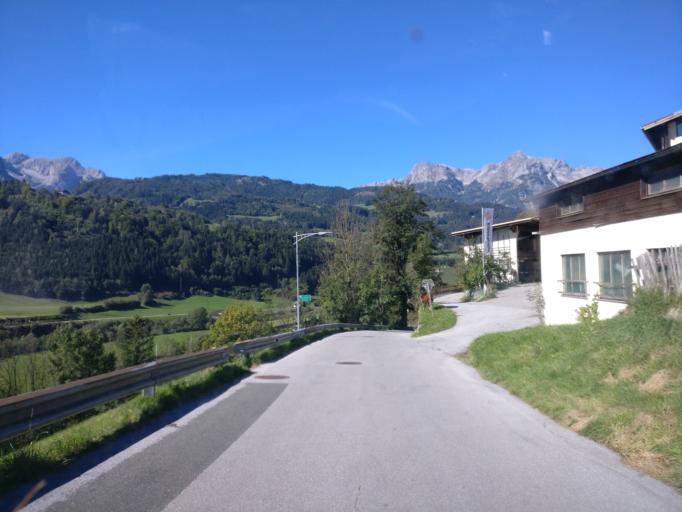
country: AT
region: Salzburg
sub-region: Politischer Bezirk Sankt Johann im Pongau
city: Pfarrwerfen
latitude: 47.4553
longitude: 13.2094
